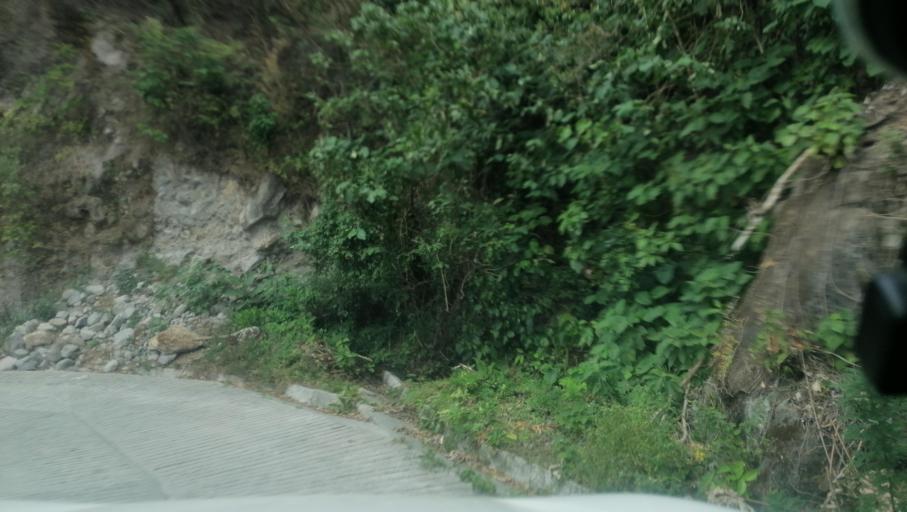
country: MX
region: Chiapas
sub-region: Cacahoatan
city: Benito Juarez
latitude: 15.1641
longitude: -92.1780
